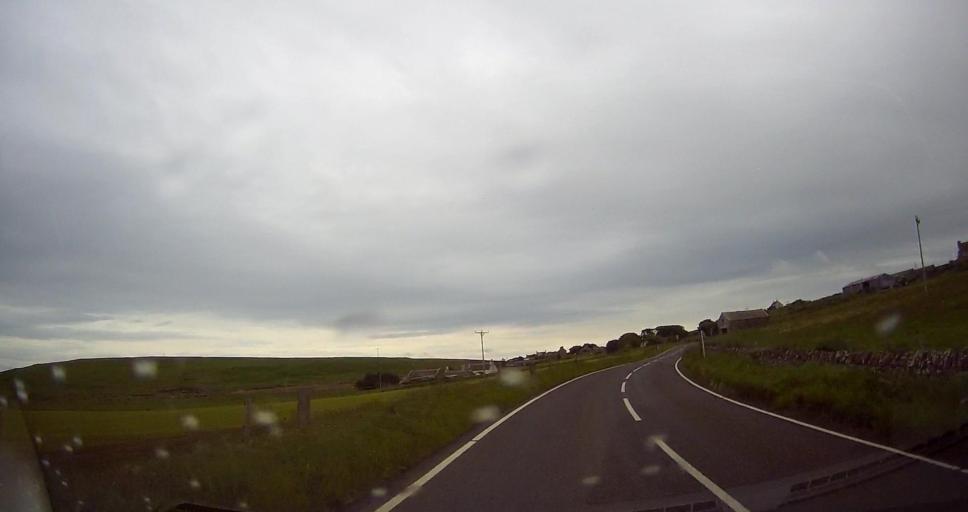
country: GB
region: Scotland
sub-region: Orkney Islands
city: Orkney
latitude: 59.1093
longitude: -3.0961
